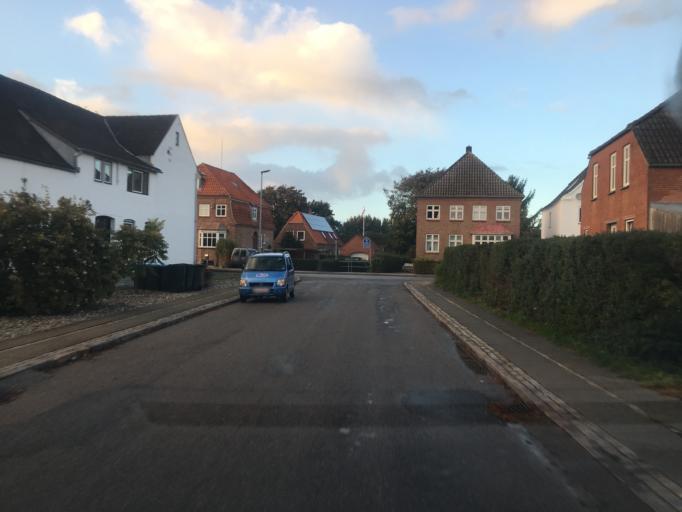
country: DK
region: South Denmark
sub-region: Tonder Kommune
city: Tonder
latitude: 54.9351
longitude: 8.8542
